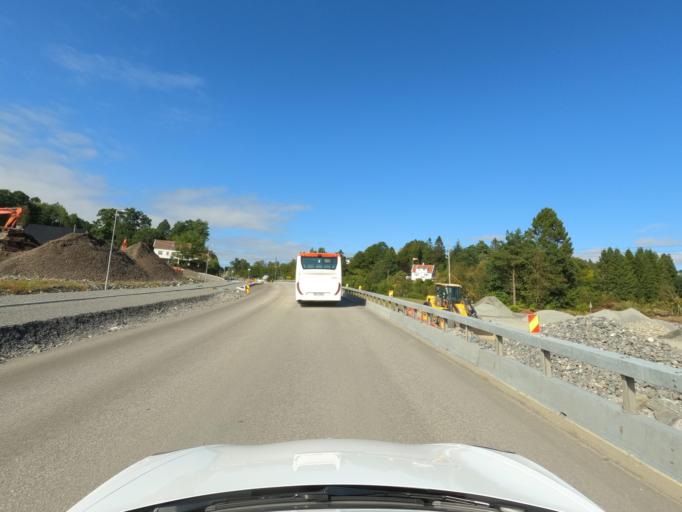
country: NO
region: Hordaland
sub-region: Bergen
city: Ytrebygda
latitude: 60.2765
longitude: 5.2516
